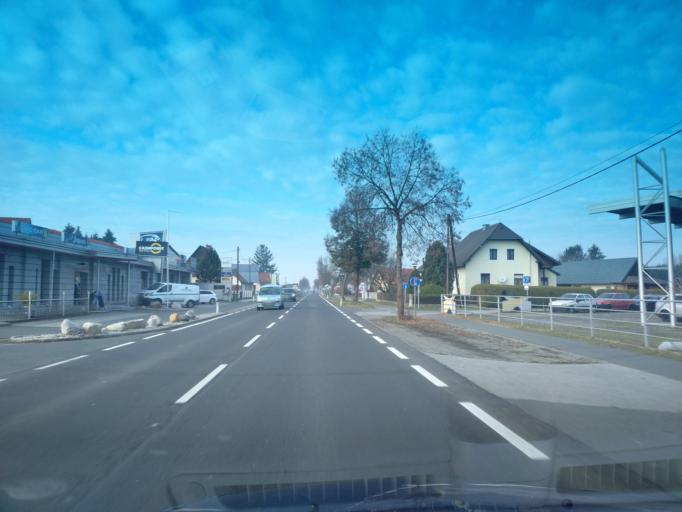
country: AT
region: Styria
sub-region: Politischer Bezirk Leibnitz
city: Sankt Veit am Vogau
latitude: 46.7327
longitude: 15.6124
